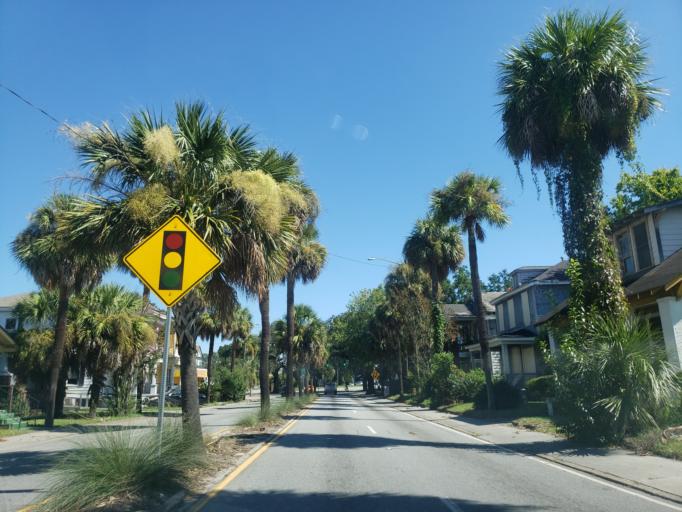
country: US
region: Georgia
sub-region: Chatham County
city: Savannah
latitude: 32.0541
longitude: -81.1082
